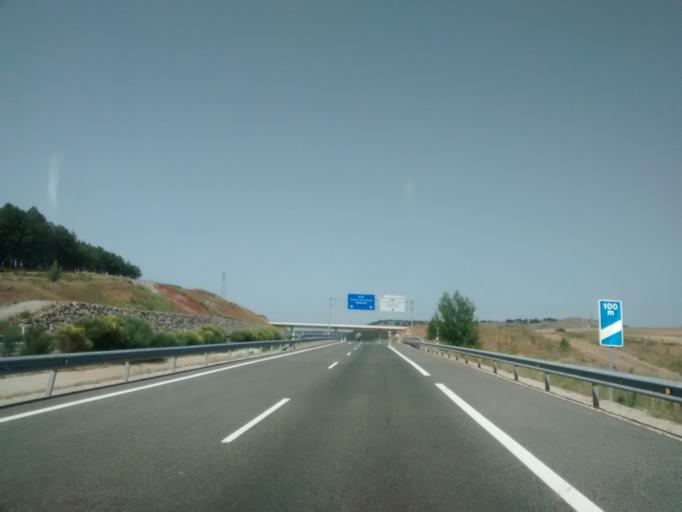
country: ES
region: Castille and Leon
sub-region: Provincia de Palencia
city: Aguilar de Campoo
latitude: 42.7715
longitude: -4.2629
